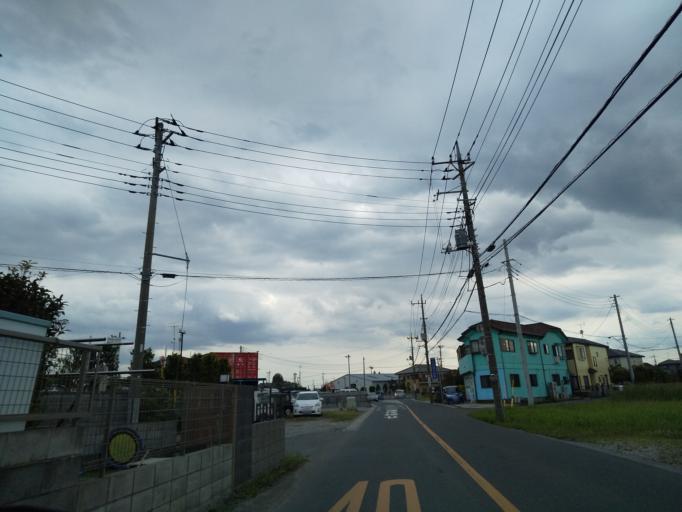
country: JP
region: Saitama
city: Kasukabe
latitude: 35.9897
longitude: 139.7830
